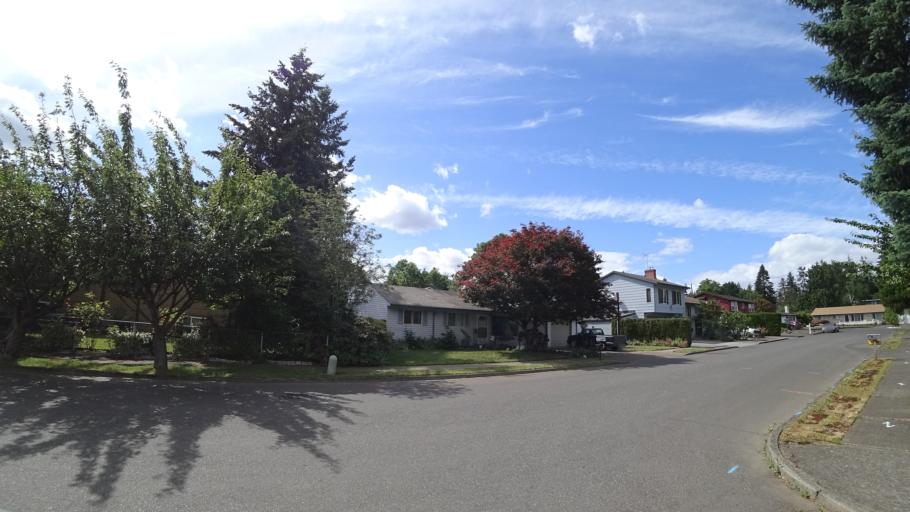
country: US
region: Oregon
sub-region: Multnomah County
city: Lents
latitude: 45.4905
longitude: -122.5423
